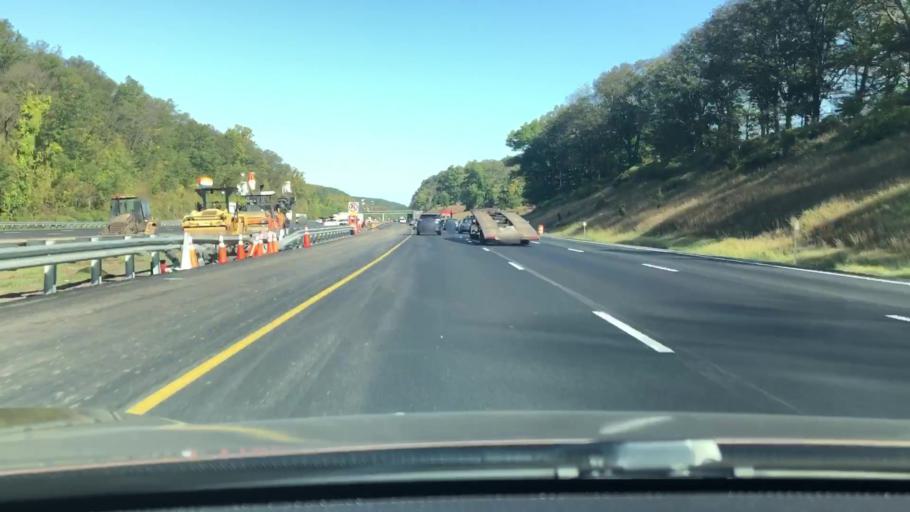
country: US
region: New York
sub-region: Orange County
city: Harriman
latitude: 41.2602
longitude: -74.1581
